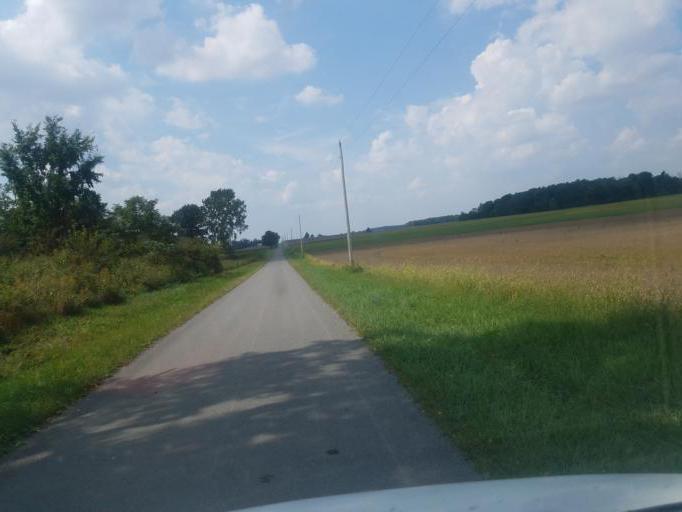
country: US
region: Ohio
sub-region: Hardin County
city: Ada
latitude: 40.6377
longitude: -83.8588
